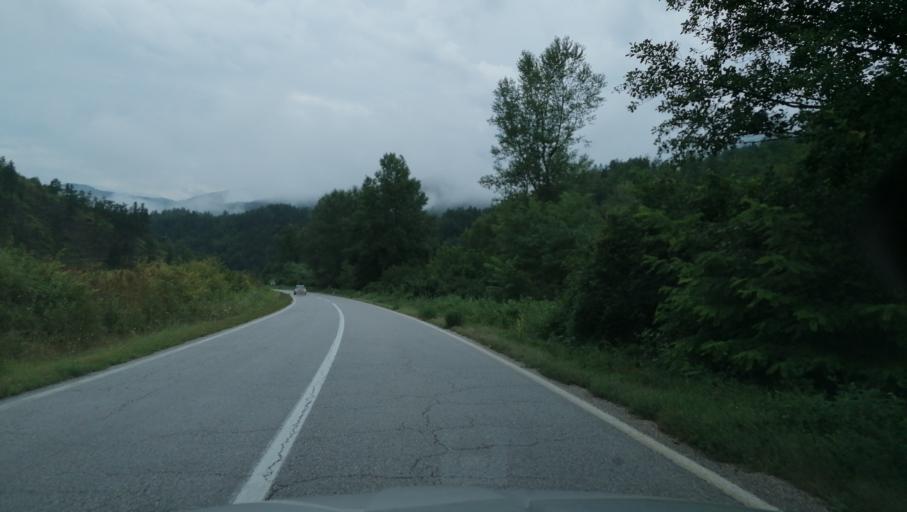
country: RS
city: Durici
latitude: 43.7703
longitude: 19.3862
